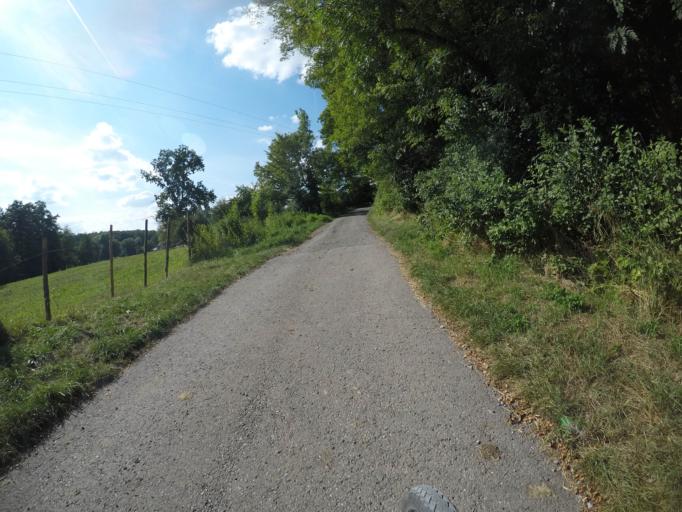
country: DE
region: Baden-Wuerttemberg
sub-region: Regierungsbezirk Stuttgart
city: Altdorf
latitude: 48.6500
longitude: 8.9770
